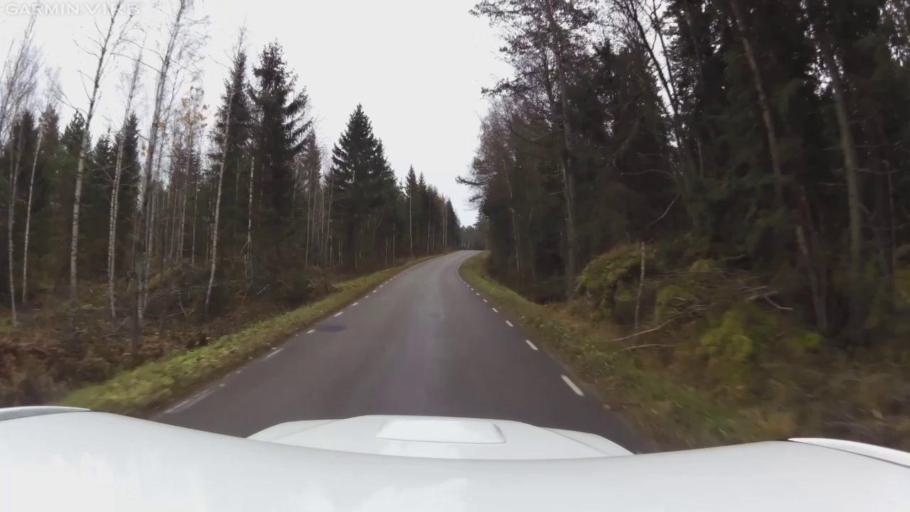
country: SE
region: OEstergoetland
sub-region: Mjolby Kommun
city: Mantorp
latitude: 58.1422
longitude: 15.3989
